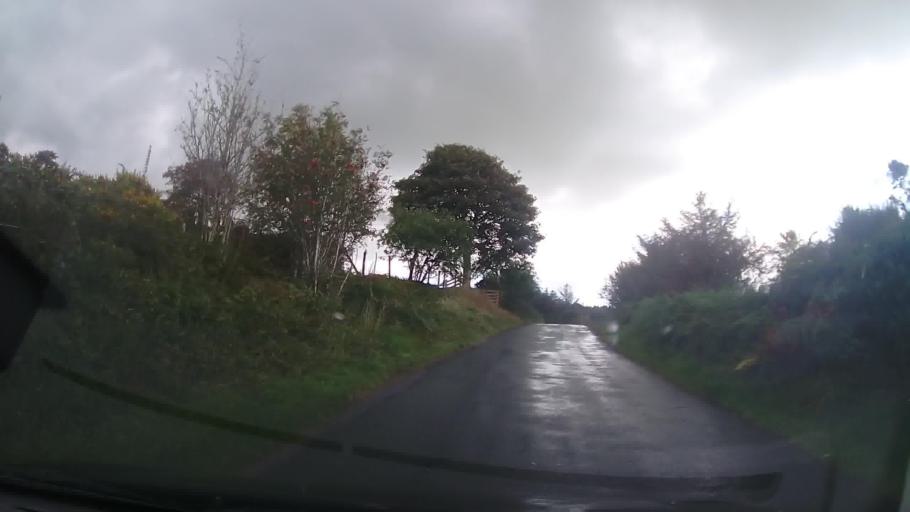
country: GB
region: England
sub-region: Shropshire
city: Norbury
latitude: 52.5763
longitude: -2.9475
